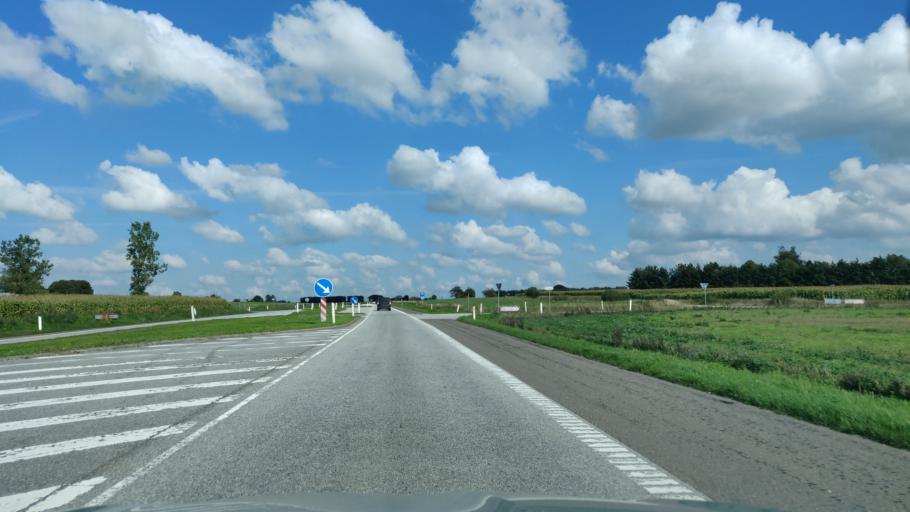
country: DK
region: North Denmark
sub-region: Vesthimmerland Kommune
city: Aars
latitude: 56.8078
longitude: 9.6511
